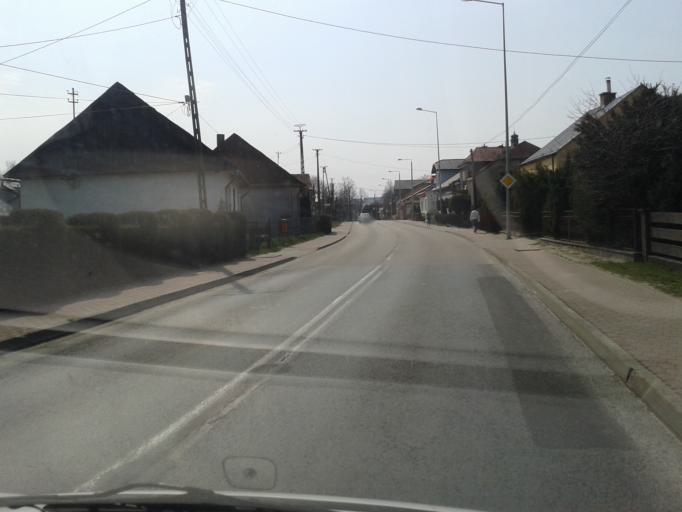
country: PL
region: Subcarpathian Voivodeship
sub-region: Powiat lubaczowski
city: Narol
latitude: 50.3514
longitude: 23.3271
